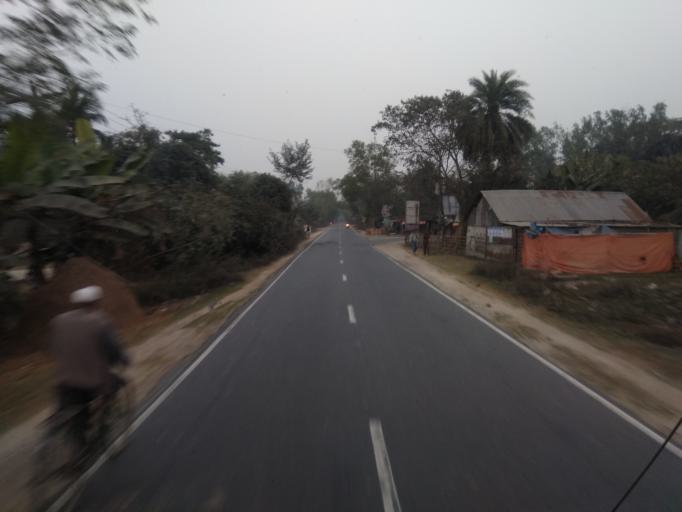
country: BD
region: Rajshahi
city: Bogra
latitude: 24.6504
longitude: 89.2580
